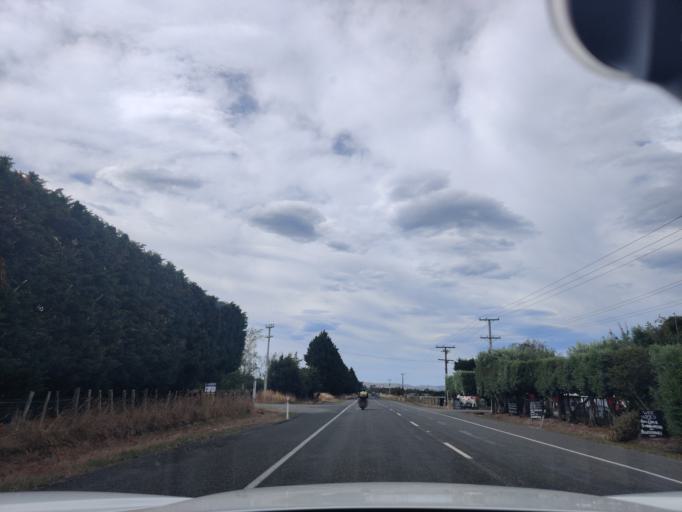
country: NZ
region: Wellington
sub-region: Masterton District
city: Masterton
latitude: -40.9008
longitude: 175.6637
